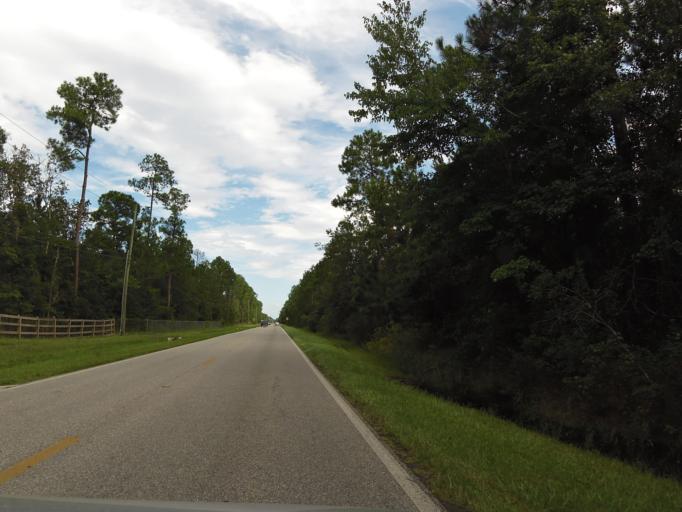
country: US
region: Florida
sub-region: Clay County
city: Asbury Lake
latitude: 30.0527
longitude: -81.7468
